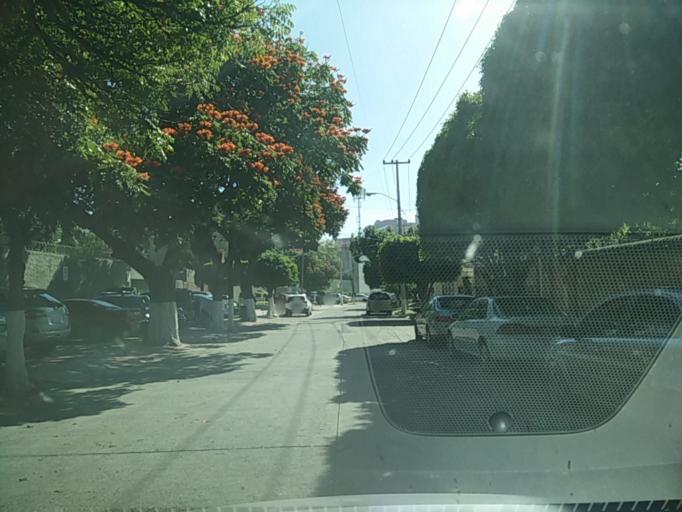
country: MX
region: Jalisco
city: Guadalajara
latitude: 20.6562
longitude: -103.3938
